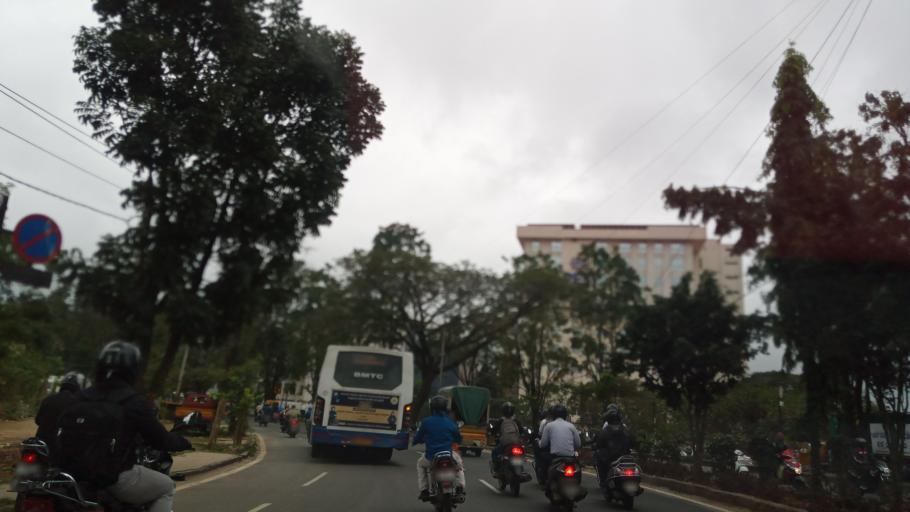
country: IN
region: Karnataka
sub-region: Bangalore Urban
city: Bangalore
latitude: 12.9369
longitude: 77.5342
